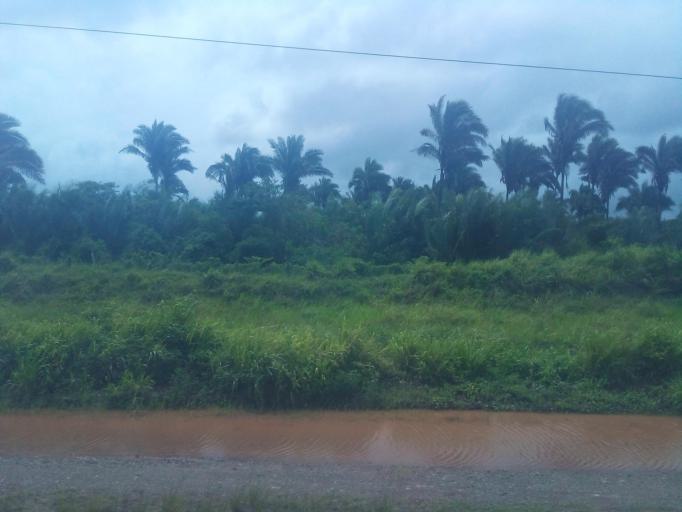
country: BR
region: Maranhao
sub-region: Arari
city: Arari
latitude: -3.5554
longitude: -44.6670
